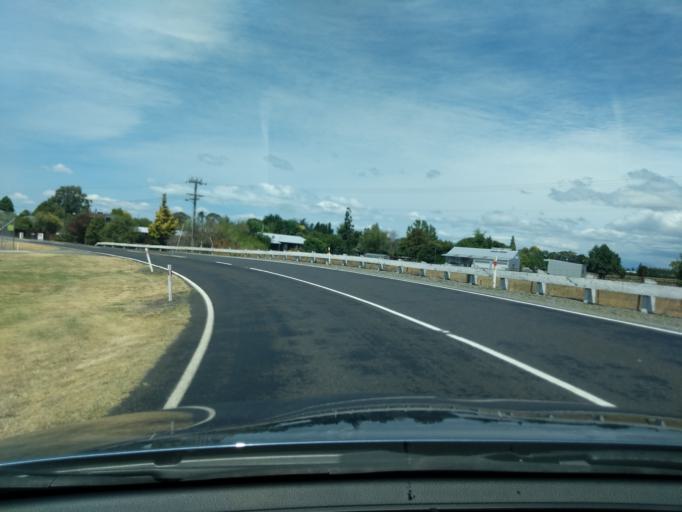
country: NZ
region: Tasman
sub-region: Tasman District
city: Motueka
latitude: -41.0757
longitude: 172.9953
